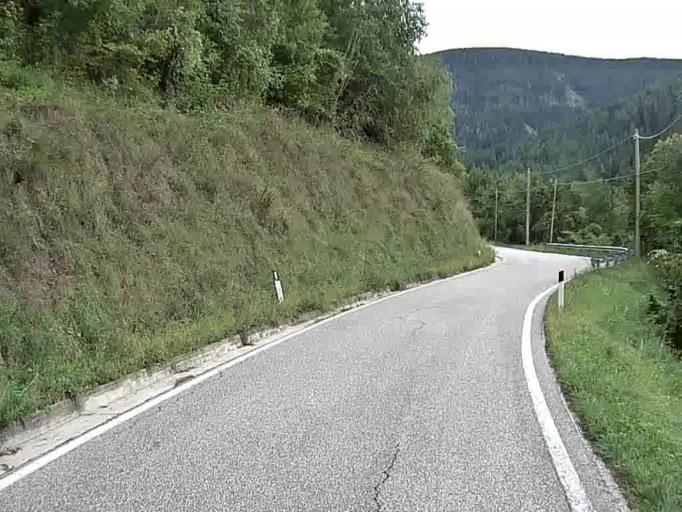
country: IT
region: Trentino-Alto Adige
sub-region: Provincia di Trento
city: Frassilongo
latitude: 46.0706
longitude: 11.2912
